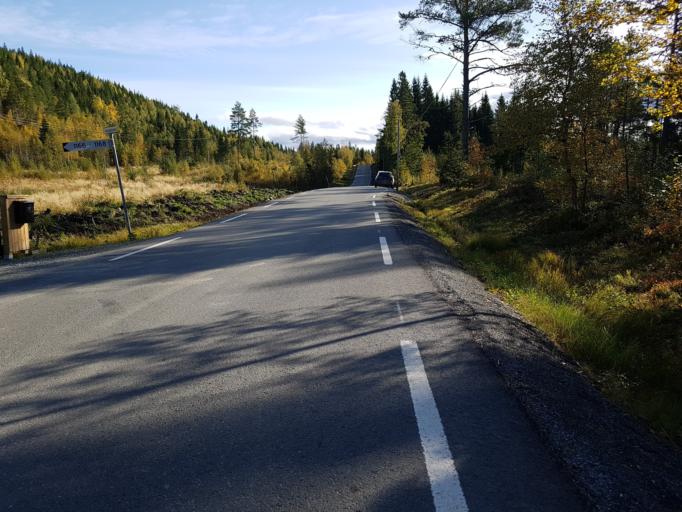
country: NO
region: Sor-Trondelag
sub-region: Malvik
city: Malvik
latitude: 63.3722
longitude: 10.6135
